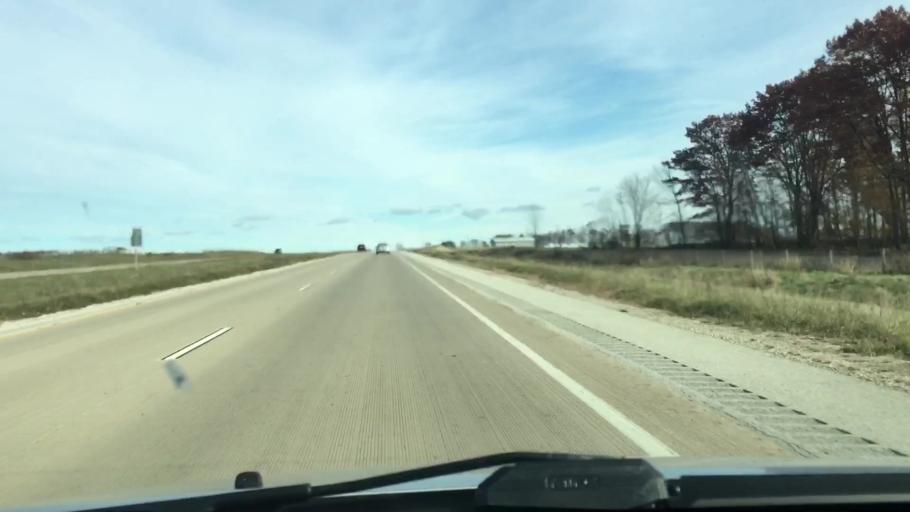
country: US
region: Wisconsin
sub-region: Kewaunee County
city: Luxemburg
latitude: 44.7166
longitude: -87.6677
